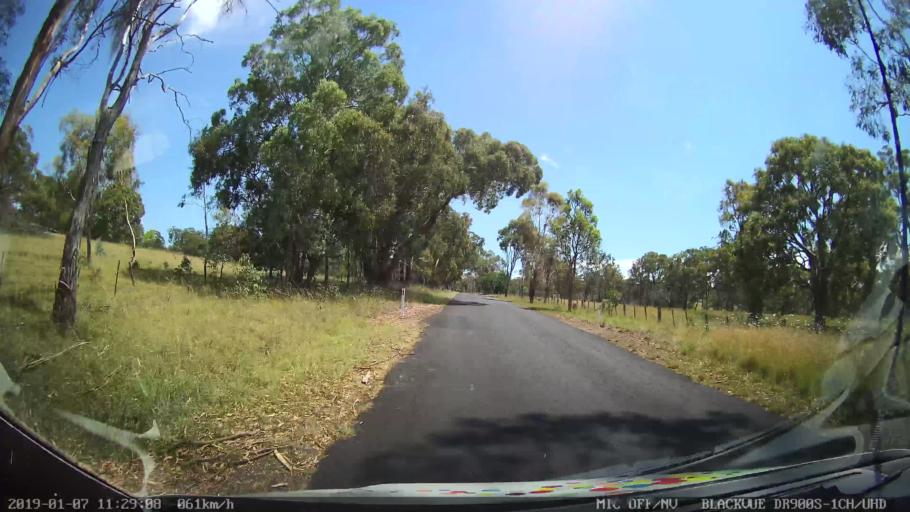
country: AU
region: New South Wales
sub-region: Armidale Dumaresq
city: Armidale
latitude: -30.4416
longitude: 151.5649
